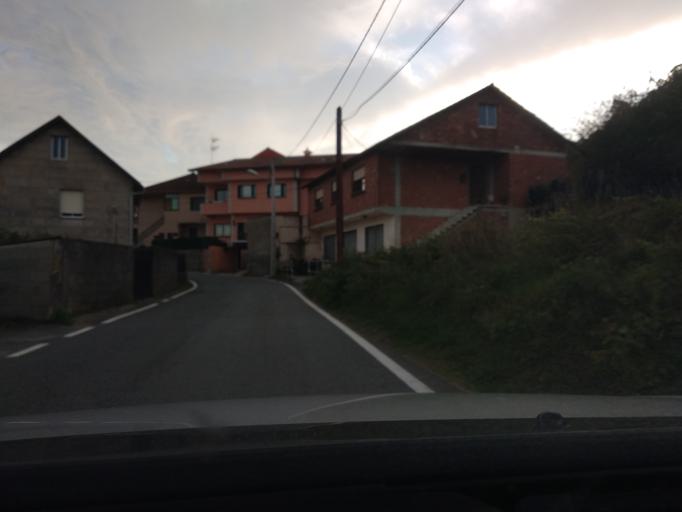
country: ES
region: Galicia
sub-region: Provincia de Pontevedra
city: Moana
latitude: 42.2901
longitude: -8.6841
